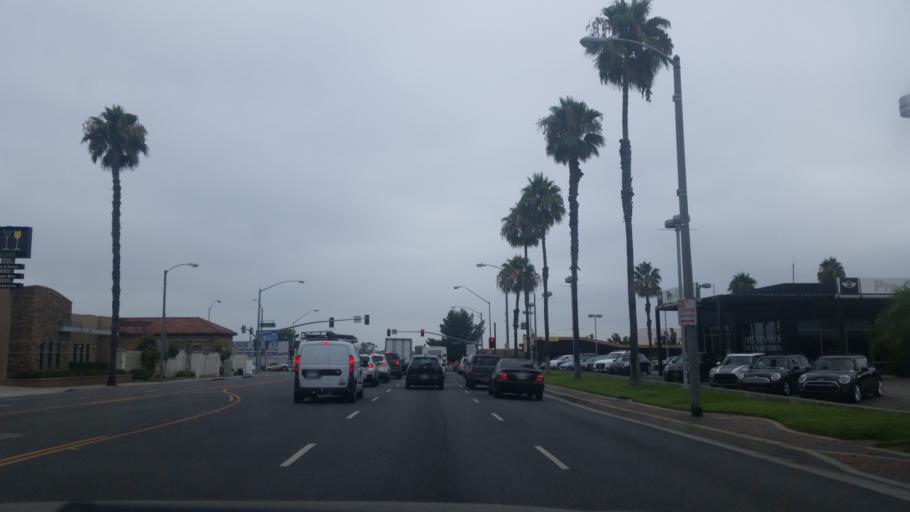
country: US
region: California
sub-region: Los Angeles County
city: Signal Hill
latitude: 33.8106
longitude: -118.1675
